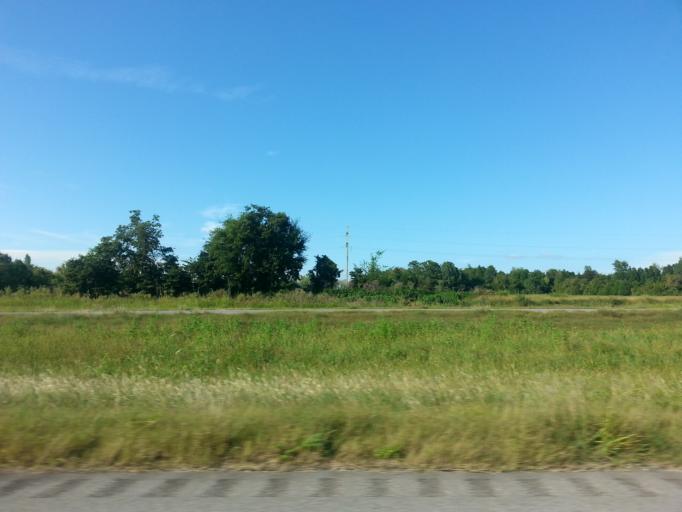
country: US
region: Alabama
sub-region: Colbert County
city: Tuscumbia
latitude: 34.7228
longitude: -87.8164
